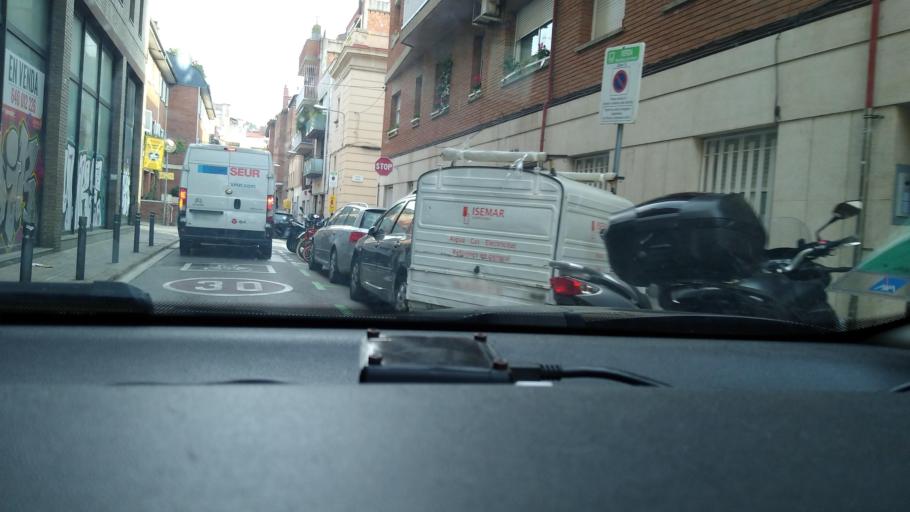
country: ES
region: Catalonia
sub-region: Provincia de Barcelona
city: Sarria-Sant Gervasi
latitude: 41.4072
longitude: 2.1455
